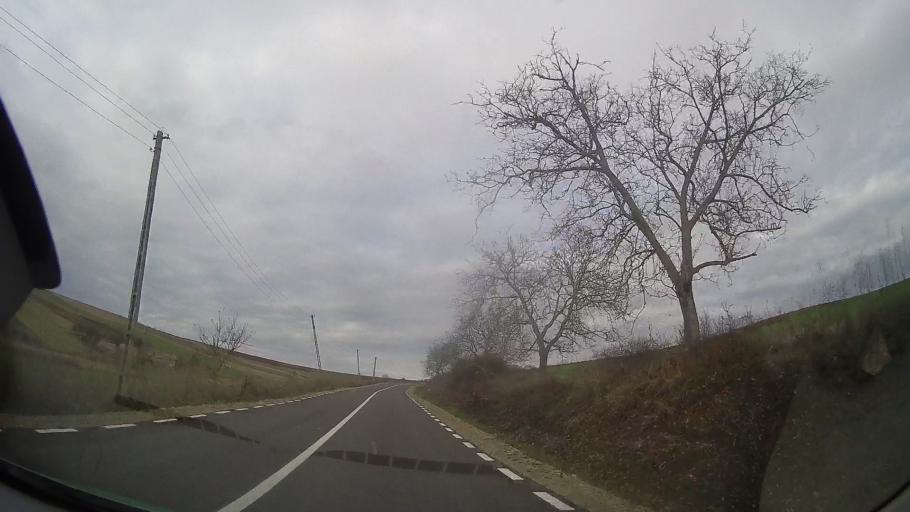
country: RO
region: Bistrita-Nasaud
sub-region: Comuna Teaca
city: Ocnita
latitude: 46.8206
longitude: 24.4850
